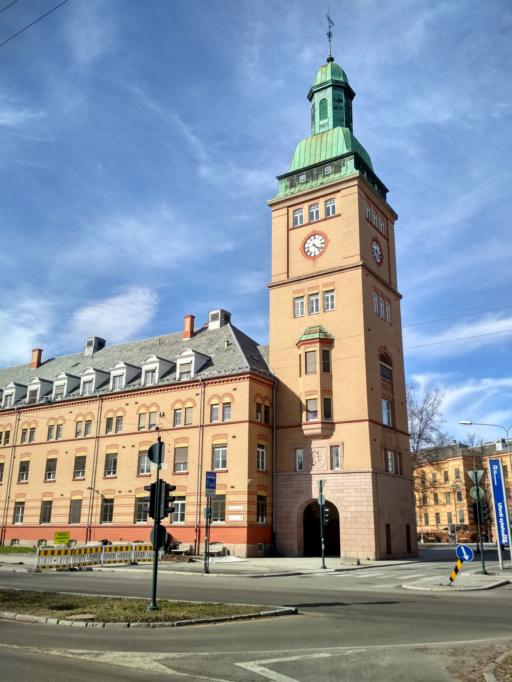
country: NO
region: Oslo
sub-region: Oslo
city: Oslo
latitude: 59.9276
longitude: 10.7410
